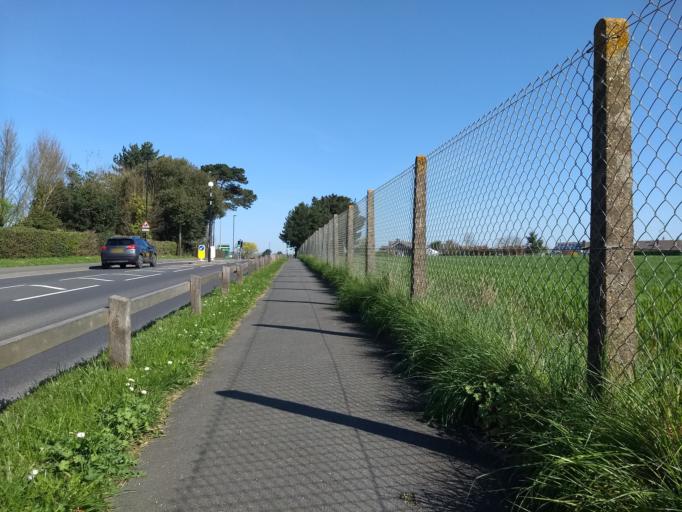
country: GB
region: England
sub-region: Isle of Wight
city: East Cowes
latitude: 50.7384
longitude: -1.2688
